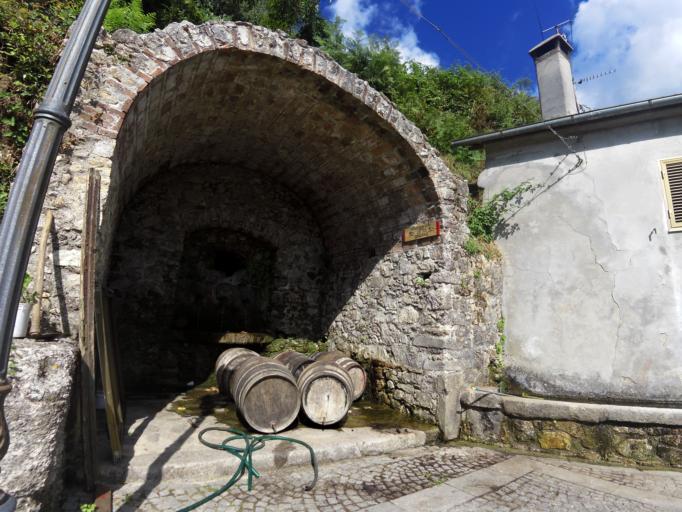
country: IT
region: Calabria
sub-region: Provincia di Vibo-Valentia
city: Mongiana
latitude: 38.5111
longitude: 16.3208
